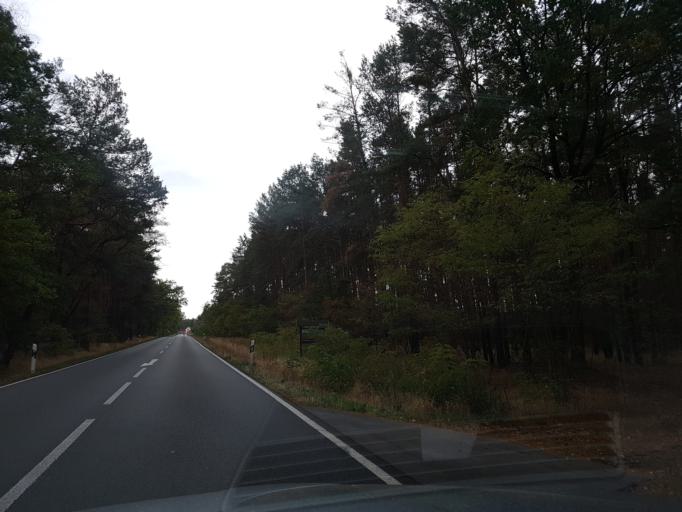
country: DE
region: Brandenburg
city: Schilda
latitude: 51.5944
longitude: 13.3562
